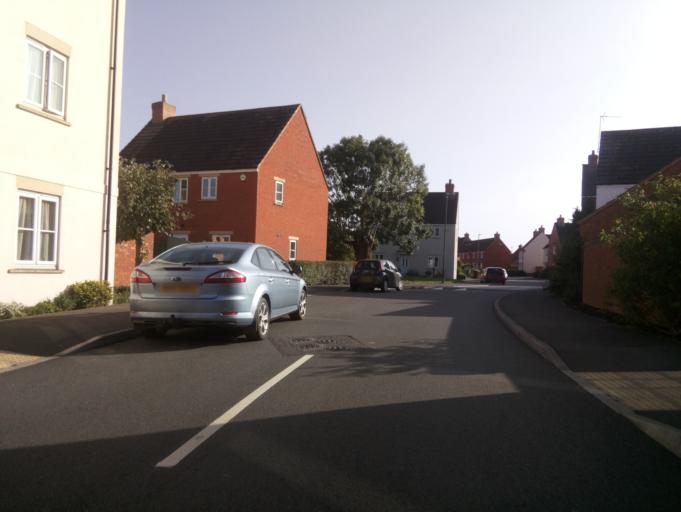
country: GB
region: England
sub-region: Gloucestershire
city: Tewkesbury
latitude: 51.9818
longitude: -2.1392
